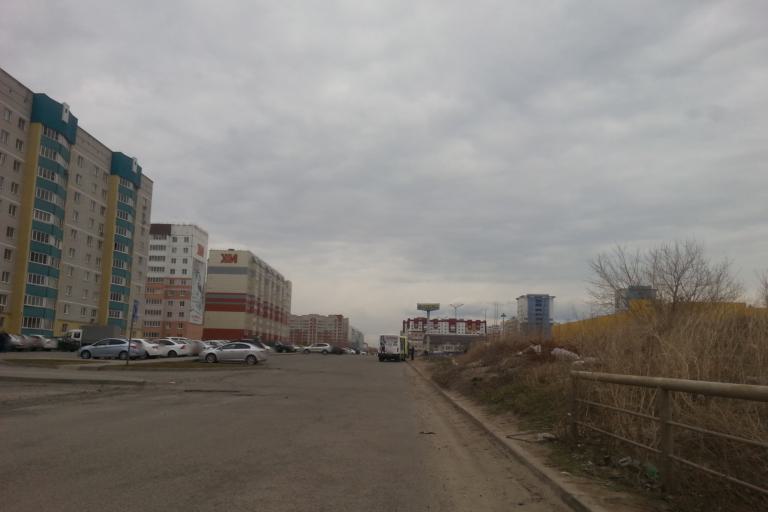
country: RU
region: Altai Krai
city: Novosilikatnyy
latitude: 53.3250
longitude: 83.6829
